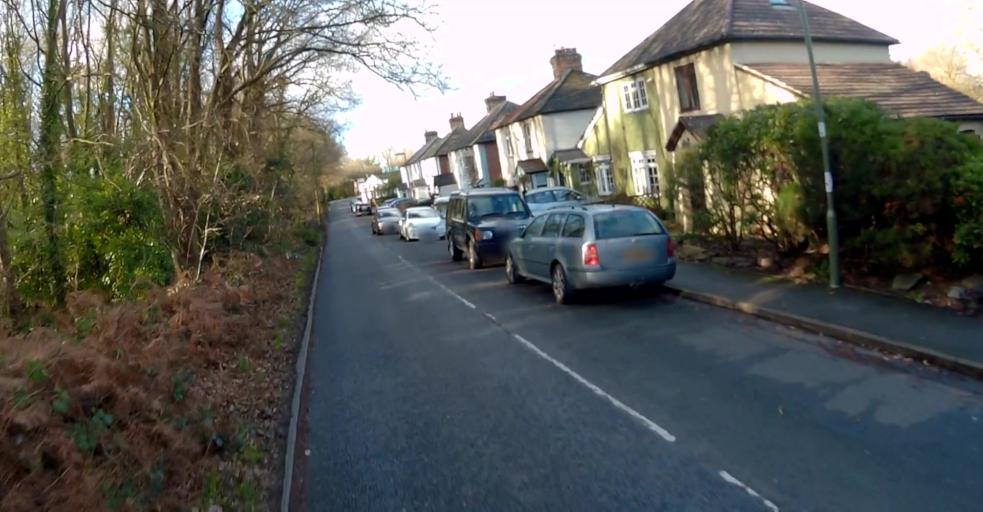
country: GB
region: England
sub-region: Surrey
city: Ottershaw
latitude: 51.3651
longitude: -0.5161
